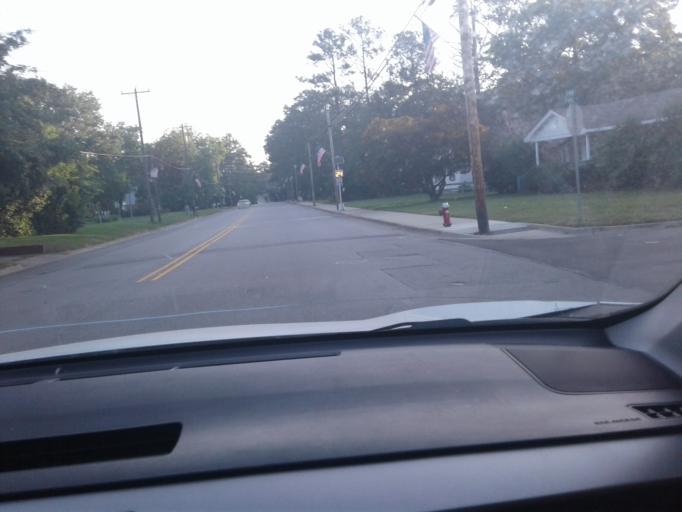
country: US
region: North Carolina
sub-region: Wake County
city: Fuquay-Varina
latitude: 35.5765
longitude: -78.8002
